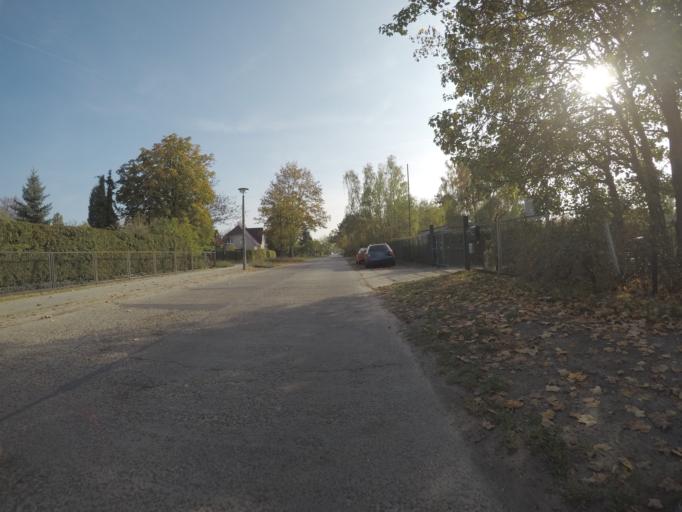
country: DE
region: Berlin
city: Altglienicke
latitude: 52.4133
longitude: 13.5444
